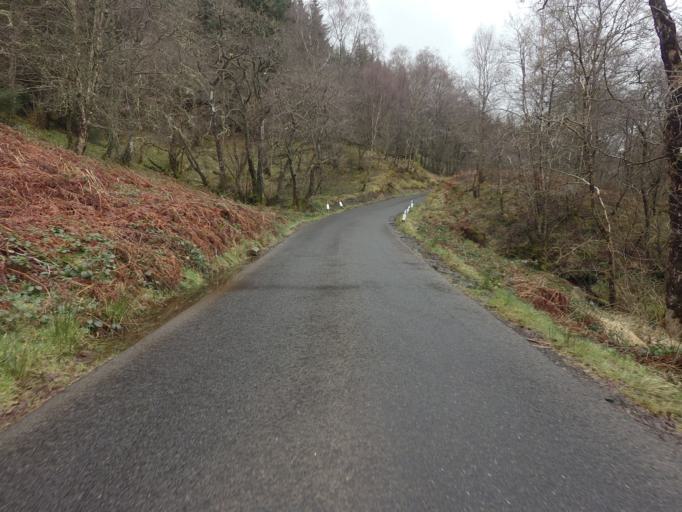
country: GB
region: Scotland
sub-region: West Dunbartonshire
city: Balloch
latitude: 56.2170
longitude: -4.5446
